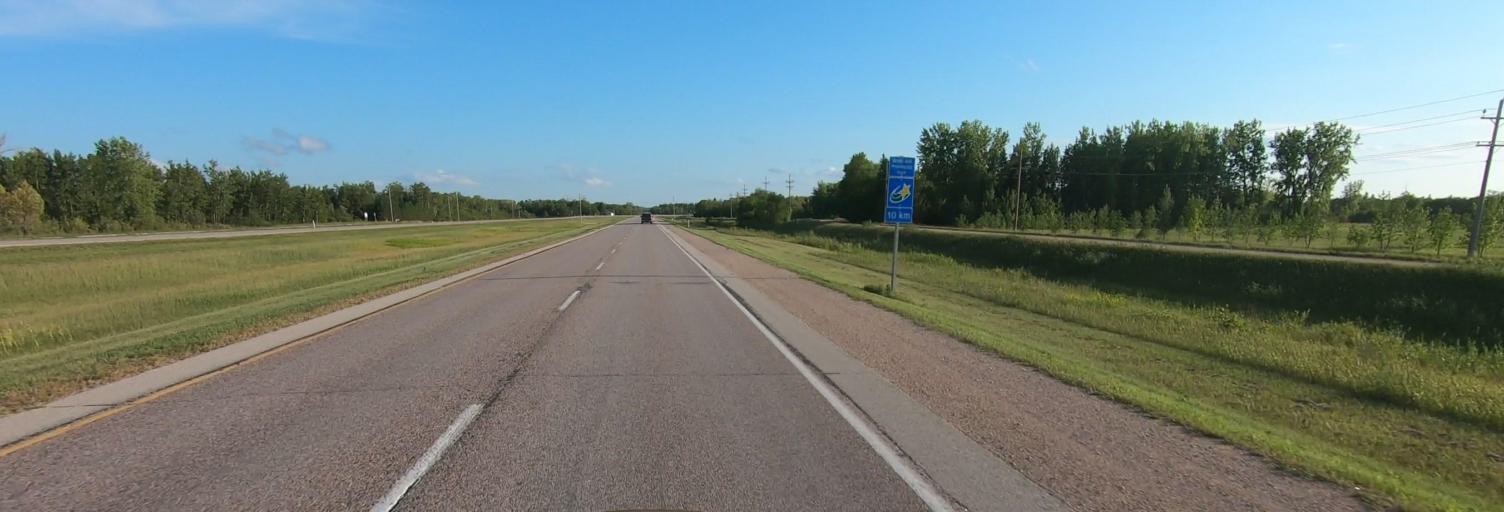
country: CA
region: Manitoba
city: Selkirk
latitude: 50.0947
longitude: -96.8642
